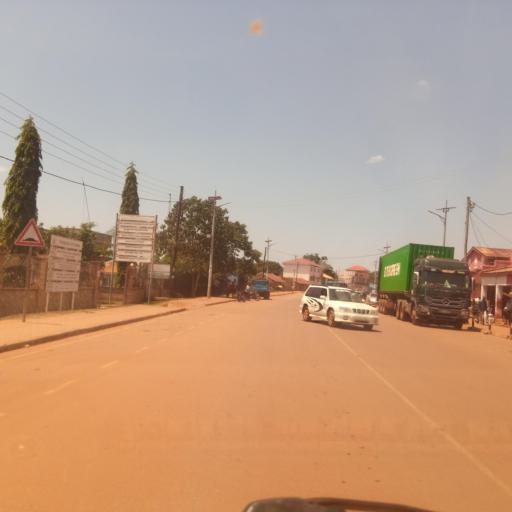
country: UG
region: Northern Region
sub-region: Lira District
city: Lira
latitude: 2.2400
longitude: 32.8913
